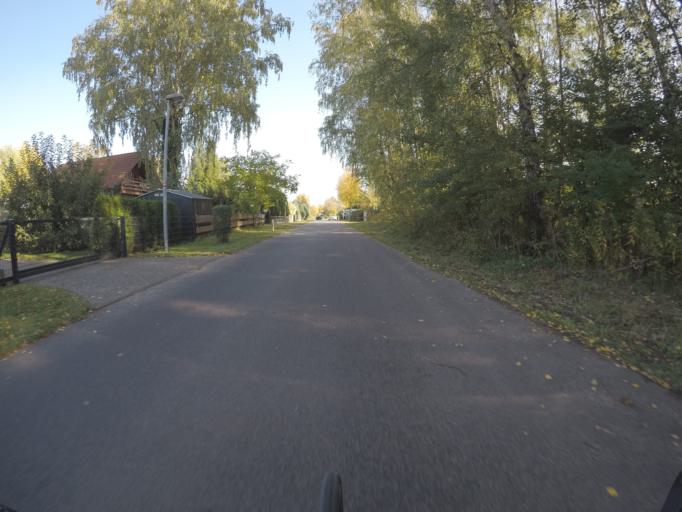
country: DE
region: Brandenburg
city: Oranienburg
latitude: 52.7236
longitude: 13.2433
